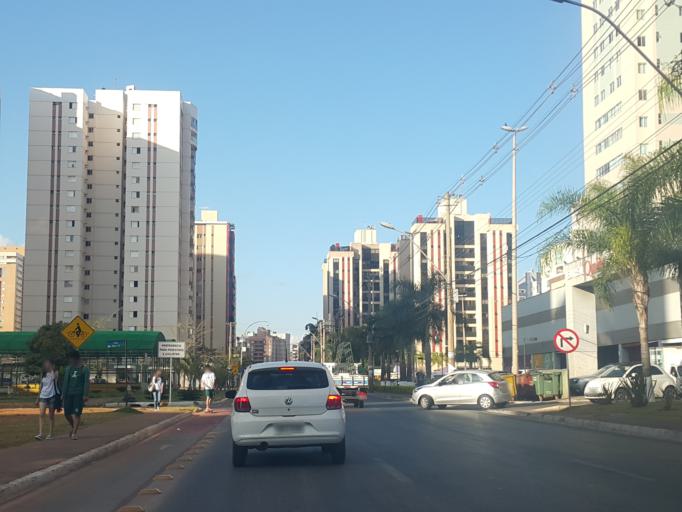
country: BR
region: Federal District
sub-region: Brasilia
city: Brasilia
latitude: -15.8395
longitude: -48.0196
